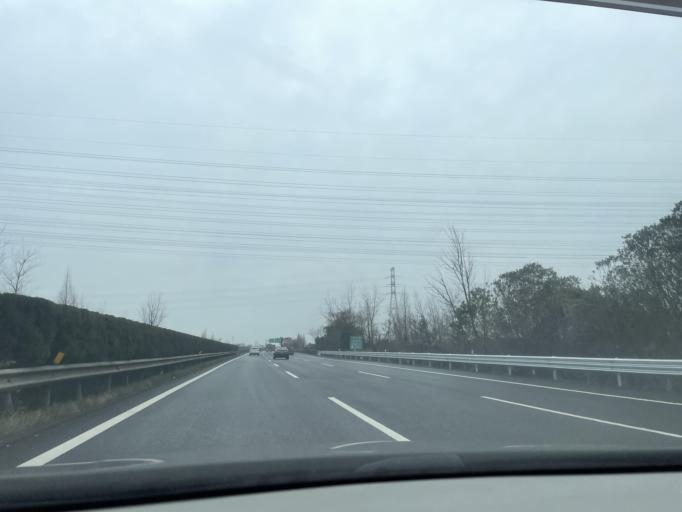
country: CN
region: Zhejiang Sheng
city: Andong
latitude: 30.2862
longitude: 121.2303
